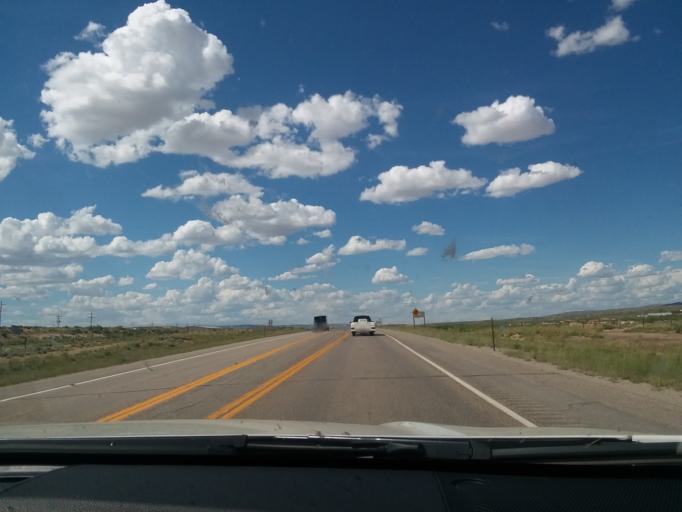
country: US
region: Wyoming
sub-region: Sweetwater County
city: North Rock Springs
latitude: 41.6579
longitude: -109.2283
